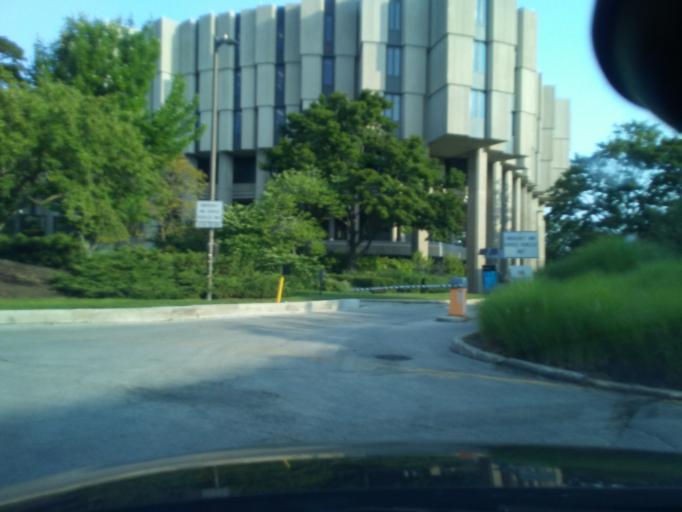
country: US
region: Illinois
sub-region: Cook County
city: Evanston
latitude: 42.0525
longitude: -87.6733
